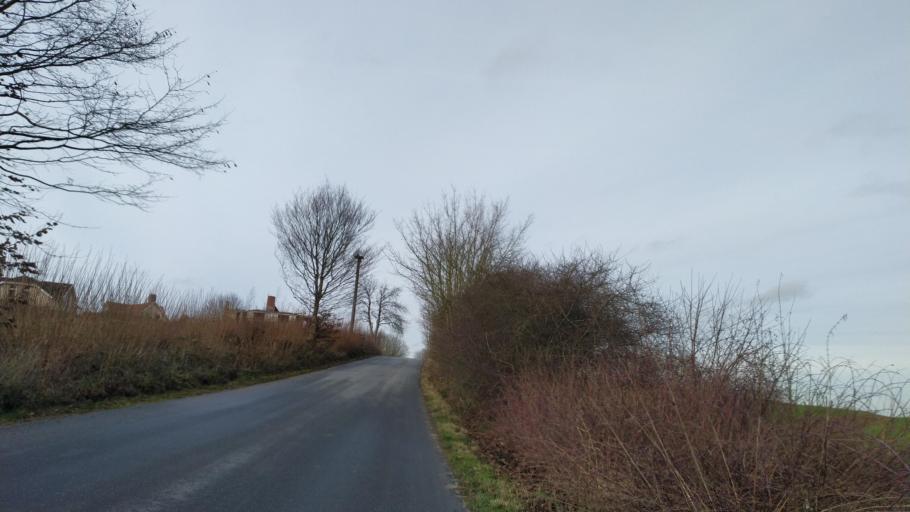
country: DE
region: Schleswig-Holstein
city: Malente
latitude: 54.1953
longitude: 10.6068
